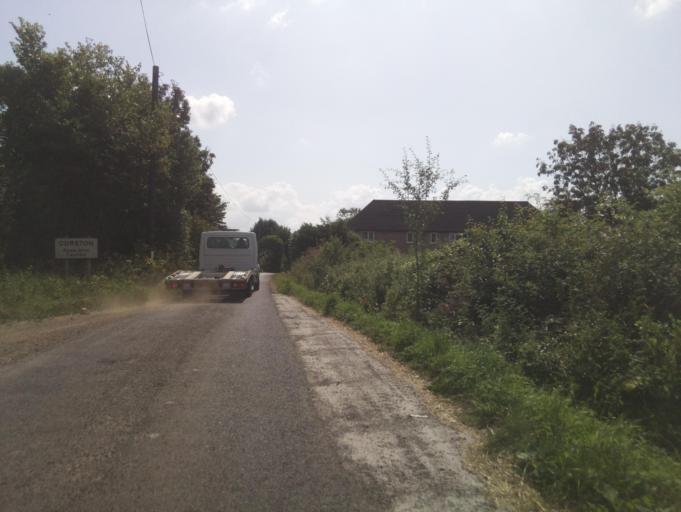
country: GB
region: England
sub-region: Wiltshire
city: Malmesbury
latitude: 51.5583
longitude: -2.1105
